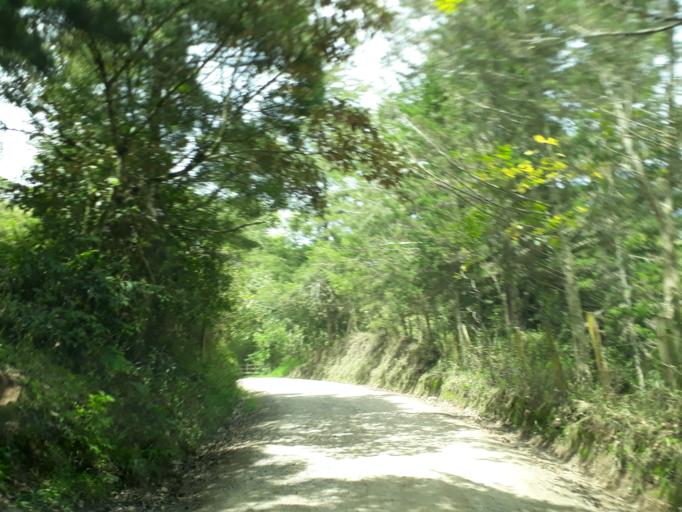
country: CO
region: Cundinamarca
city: Macheta
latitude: 5.0855
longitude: -73.5741
